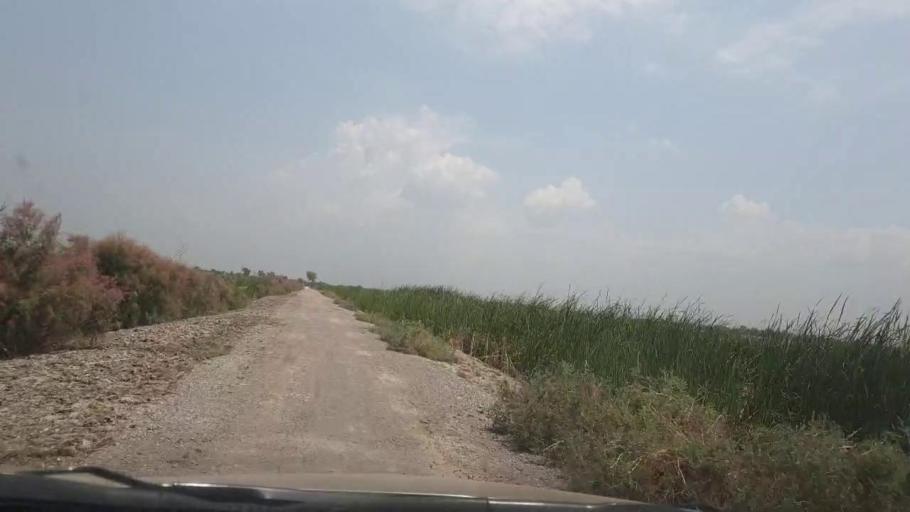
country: PK
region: Sindh
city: Naudero
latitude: 27.7224
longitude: 68.3236
